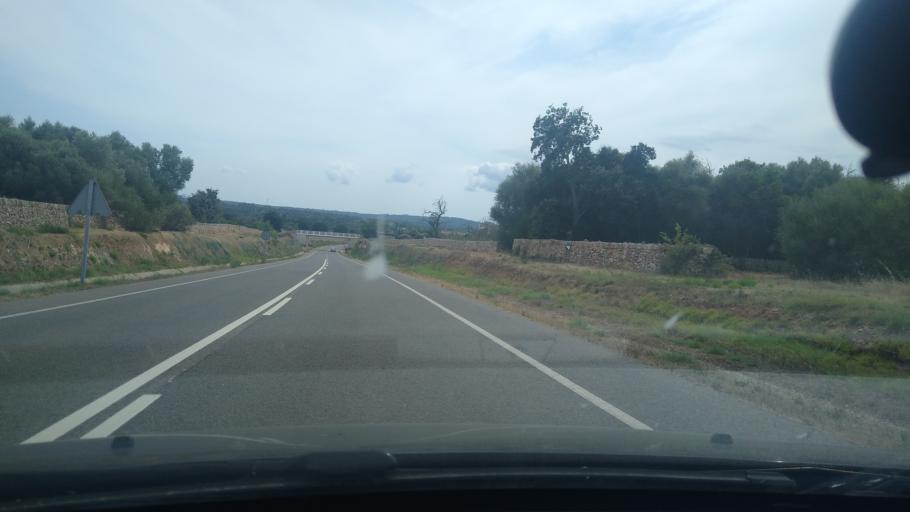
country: ES
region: Balearic Islands
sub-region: Illes Balears
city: Llubi
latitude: 39.6995
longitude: 3.0144
